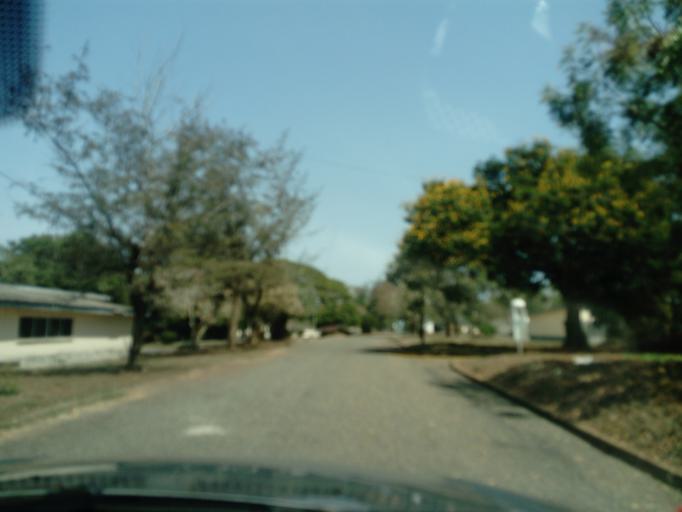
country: GH
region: Central
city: Cape Coast
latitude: 5.1102
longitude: -1.2839
